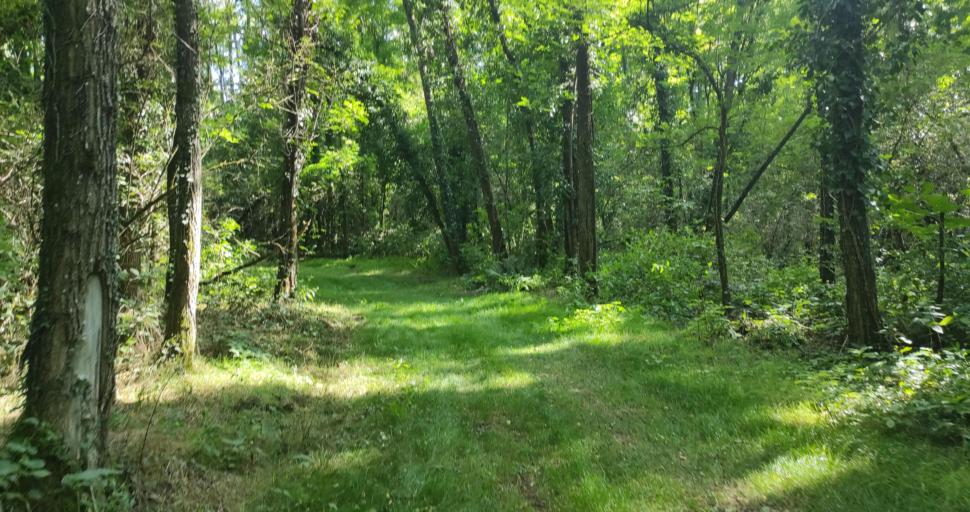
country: FR
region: Midi-Pyrenees
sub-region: Departement de l'Aveyron
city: Cransac
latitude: 44.5358
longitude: 2.2725
